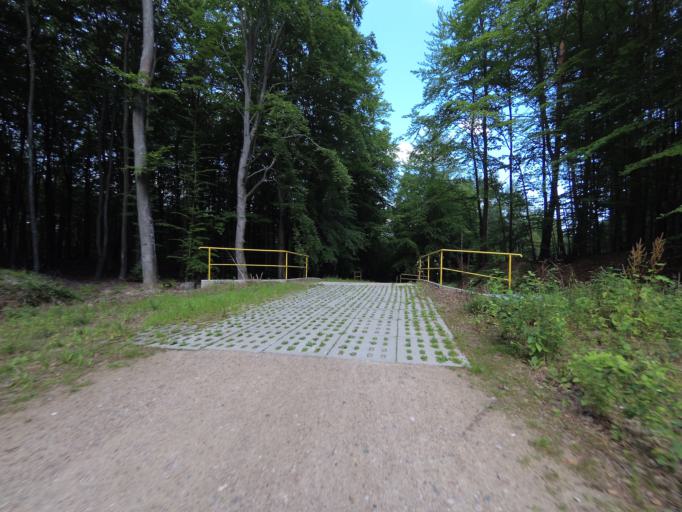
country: PL
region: Pomeranian Voivodeship
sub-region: Gdynia
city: Wielki Kack
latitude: 54.4814
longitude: 18.5012
